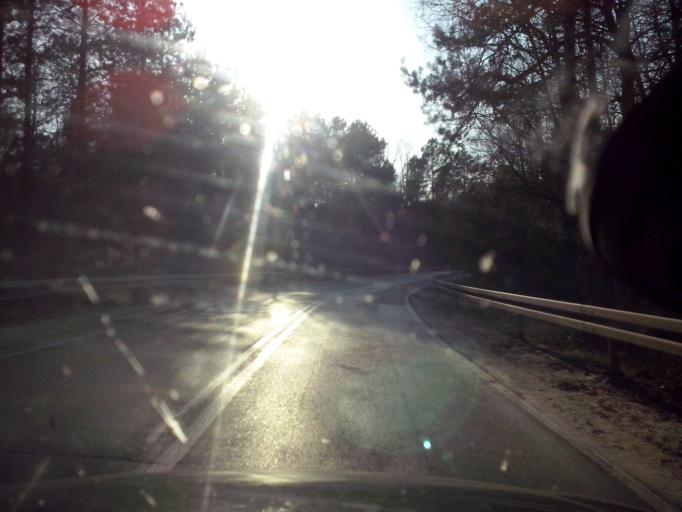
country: PL
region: Lublin Voivodeship
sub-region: Powiat janowski
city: Potok Wielki
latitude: 50.7451
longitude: 22.2154
